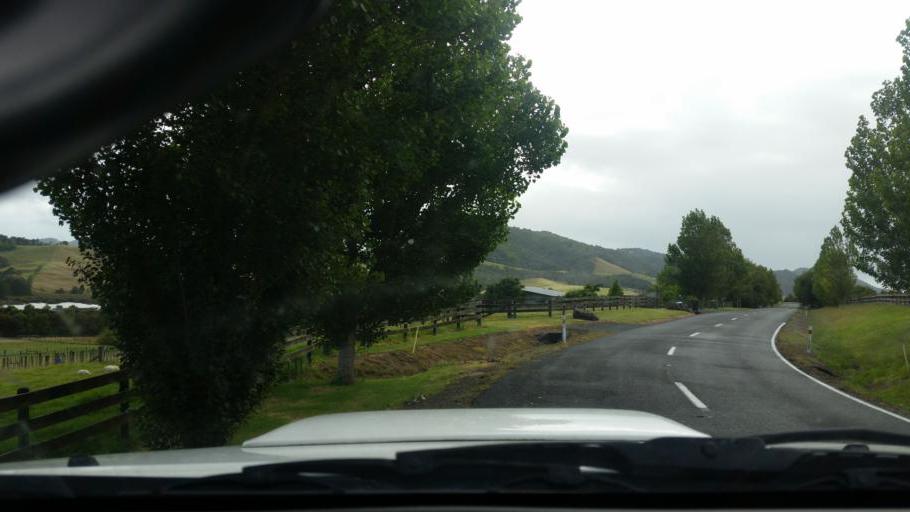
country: NZ
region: Auckland
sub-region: Auckland
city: Wellsford
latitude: -36.1307
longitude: 174.3665
